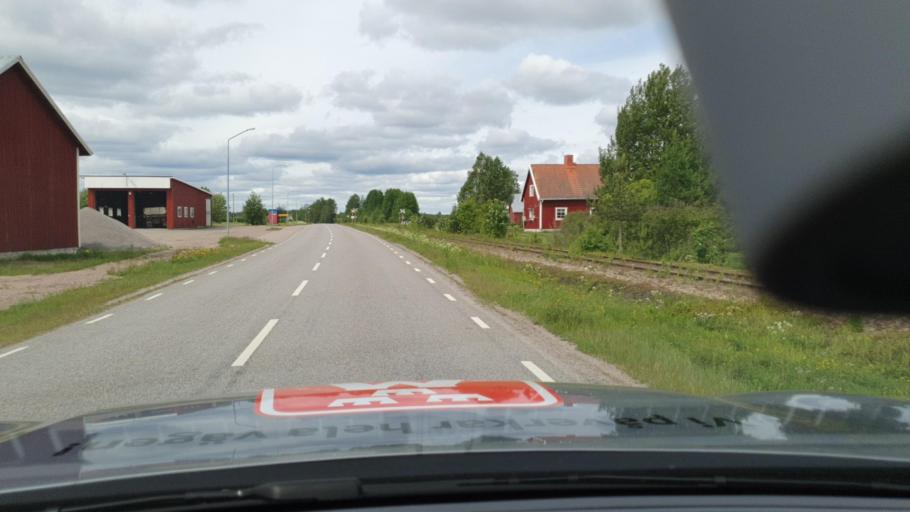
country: FI
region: Lapland
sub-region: Torniolaakso
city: Ylitornio
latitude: 66.0450
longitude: 23.6471
